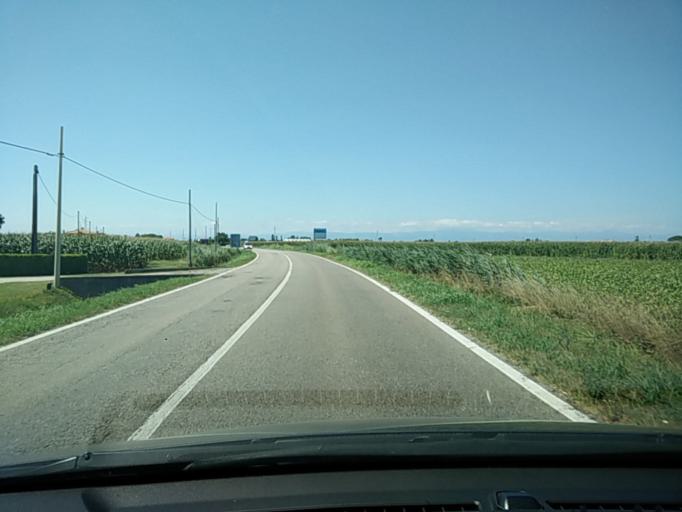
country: IT
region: Veneto
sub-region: Provincia di Venezia
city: Caorle
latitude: 45.6335
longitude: 12.8583
